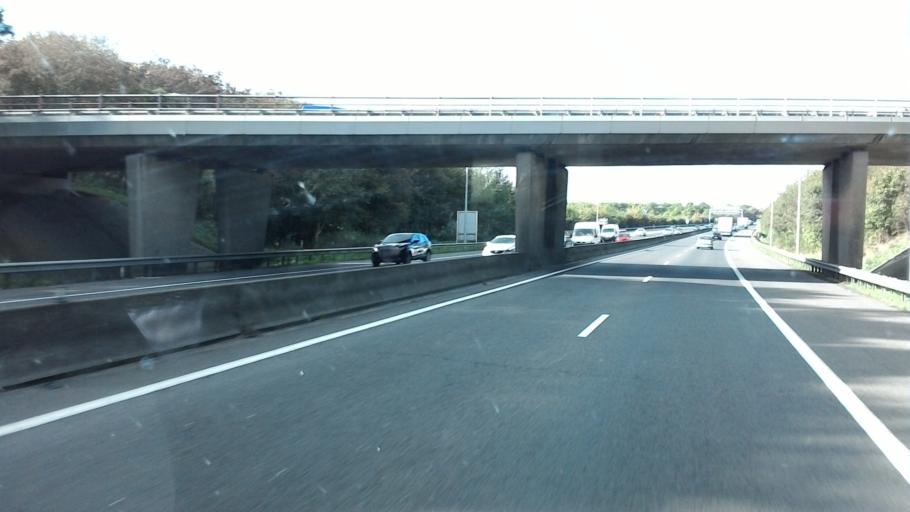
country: LU
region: Luxembourg
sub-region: Canton d'Esch-sur-Alzette
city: Dudelange
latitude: 49.4846
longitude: 6.1181
